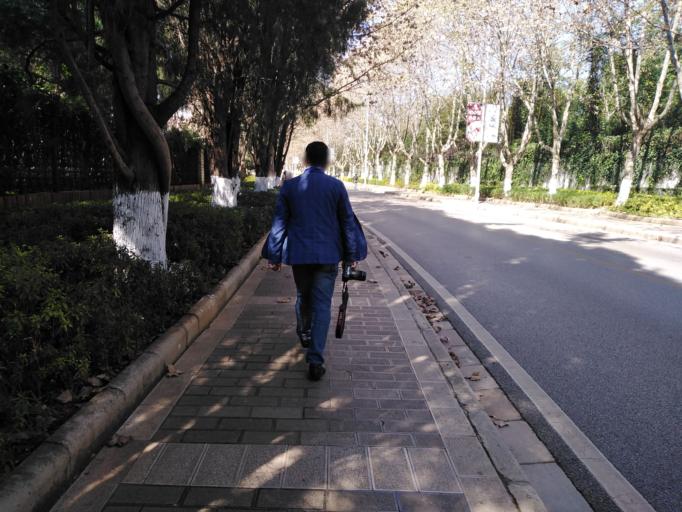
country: CN
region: Yunnan
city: Gaoyao
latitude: 24.9846
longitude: 102.6554
